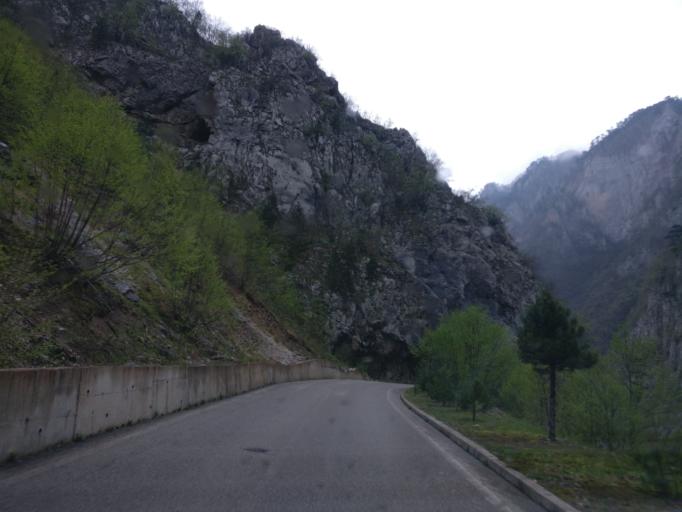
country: ME
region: Opstina Pluzine
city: Pluzine
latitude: 43.2765
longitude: 18.8478
